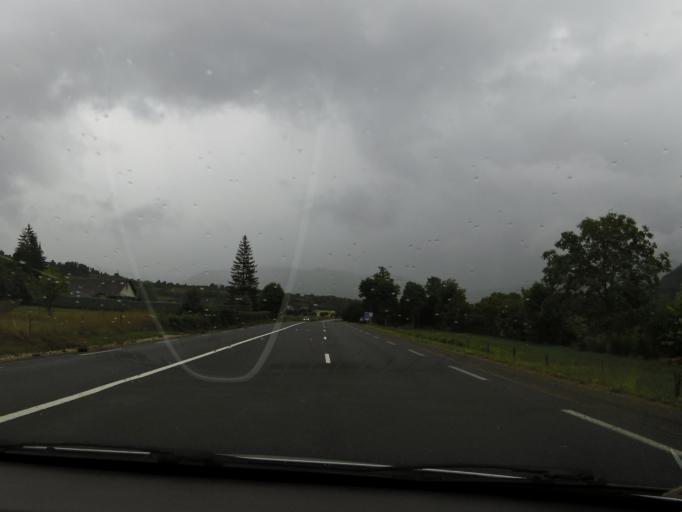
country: FR
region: Languedoc-Roussillon
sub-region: Departement de la Lozere
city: Chanac
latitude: 44.4790
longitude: 3.3253
